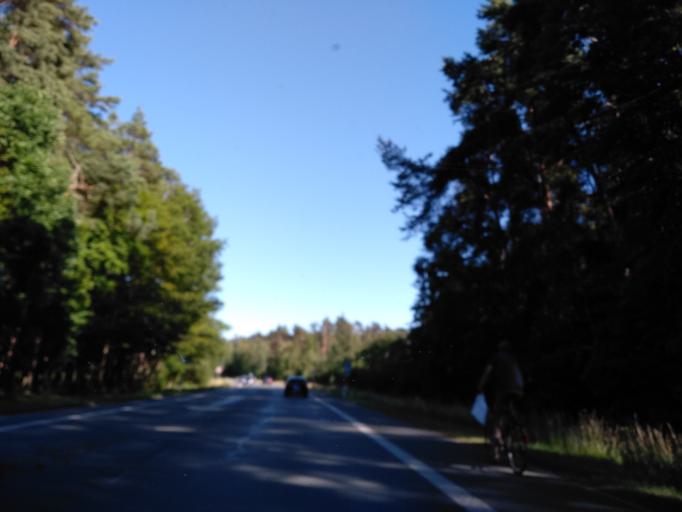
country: DE
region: Bavaria
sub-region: Regierungsbezirk Mittelfranken
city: Hessdorf
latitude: 49.6194
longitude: 10.9520
